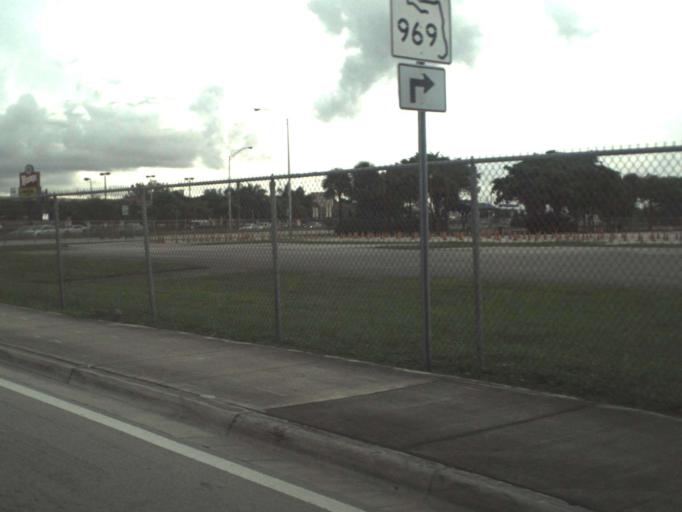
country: US
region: Florida
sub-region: Miami-Dade County
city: Flagami
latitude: 25.7827
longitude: -80.3172
